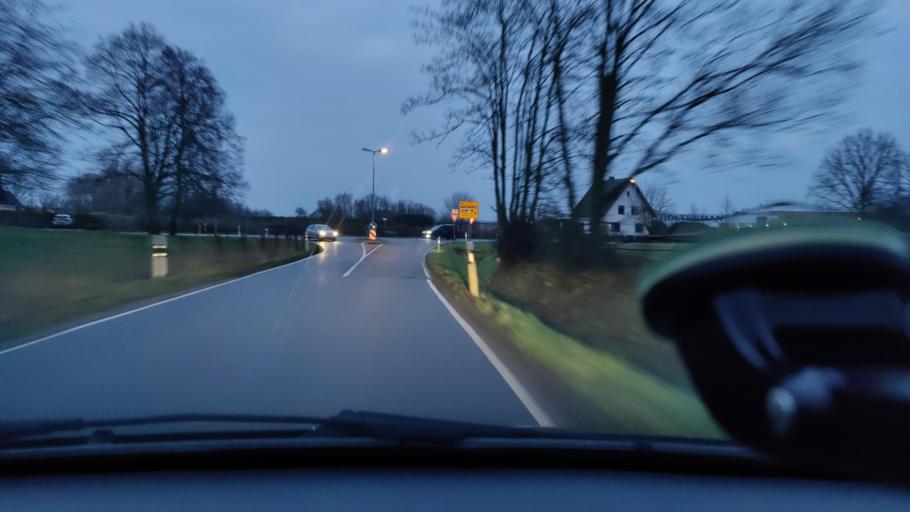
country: DE
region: North Rhine-Westphalia
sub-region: Regierungsbezirk Dusseldorf
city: Xanten
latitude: 51.6599
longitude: 6.4304
